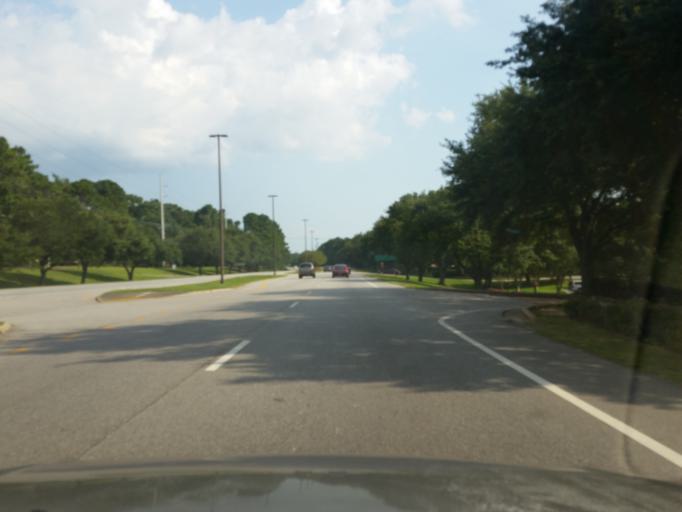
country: US
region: Alabama
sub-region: Baldwin County
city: Spanish Fort
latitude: 30.6414
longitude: -87.9128
